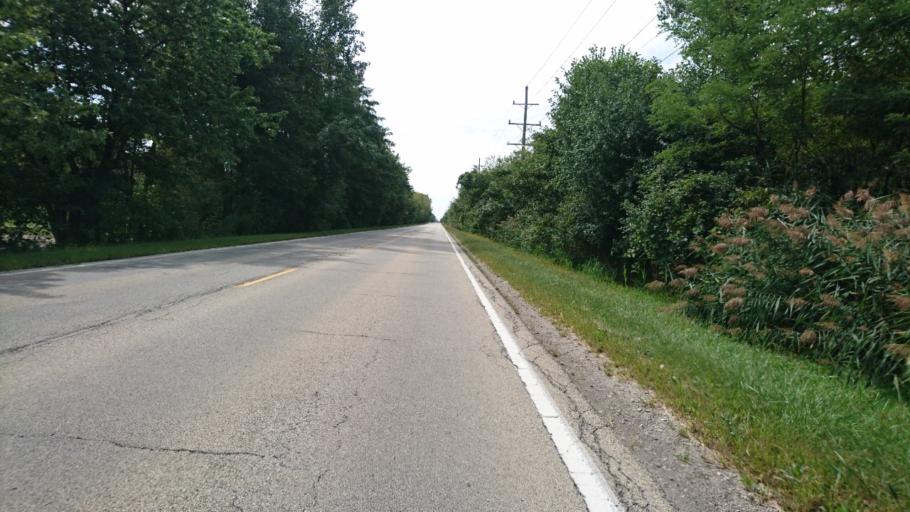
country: US
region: Illinois
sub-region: Will County
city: Braidwood
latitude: 41.2789
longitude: -88.1930
